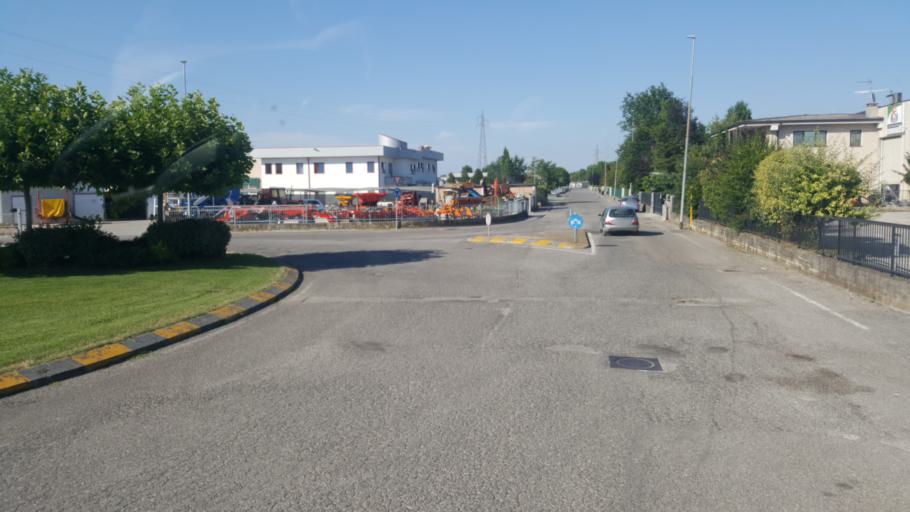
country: IT
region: Lombardy
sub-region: Provincia di Mantova
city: Asola
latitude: 45.2174
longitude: 10.3960
